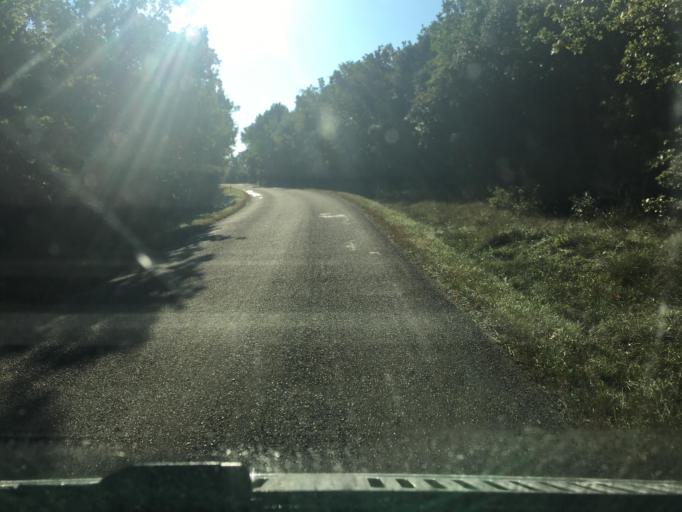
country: FR
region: Languedoc-Roussillon
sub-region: Departement du Gard
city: Goudargues
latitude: 44.1731
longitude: 4.3436
